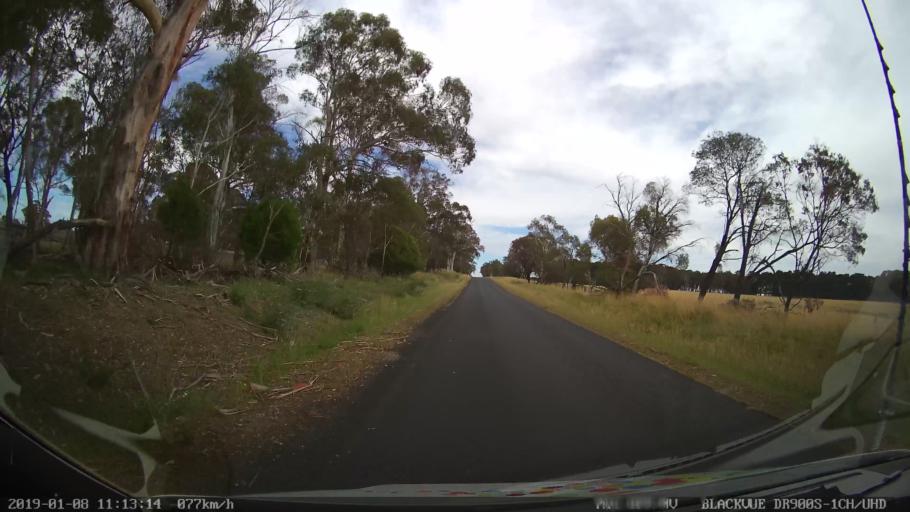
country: AU
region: New South Wales
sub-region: Guyra
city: Guyra
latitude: -30.2302
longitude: 151.6033
